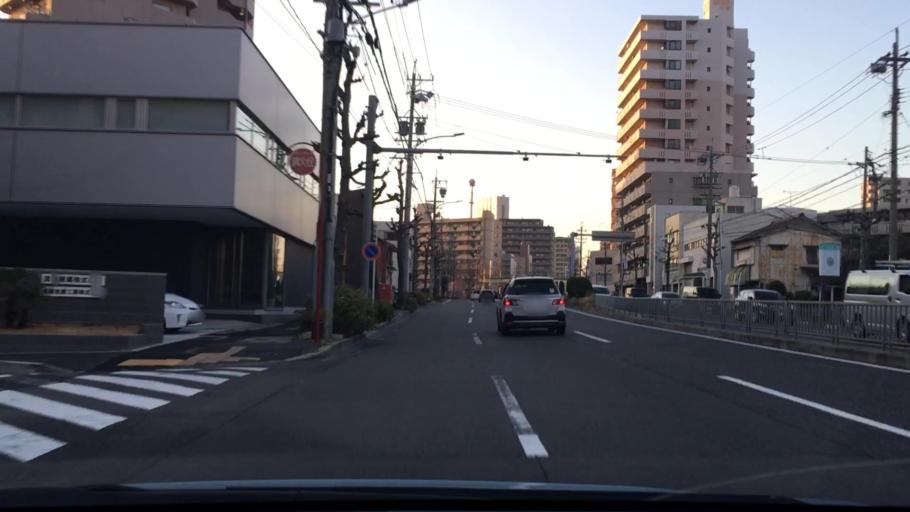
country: JP
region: Aichi
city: Nagoya-shi
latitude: 35.1345
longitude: 136.9065
